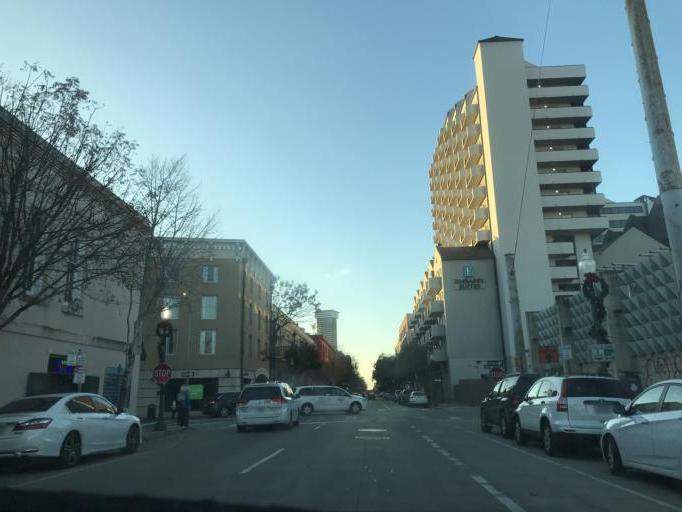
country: US
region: Louisiana
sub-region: Orleans Parish
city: New Orleans
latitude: 29.9445
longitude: -90.0654
